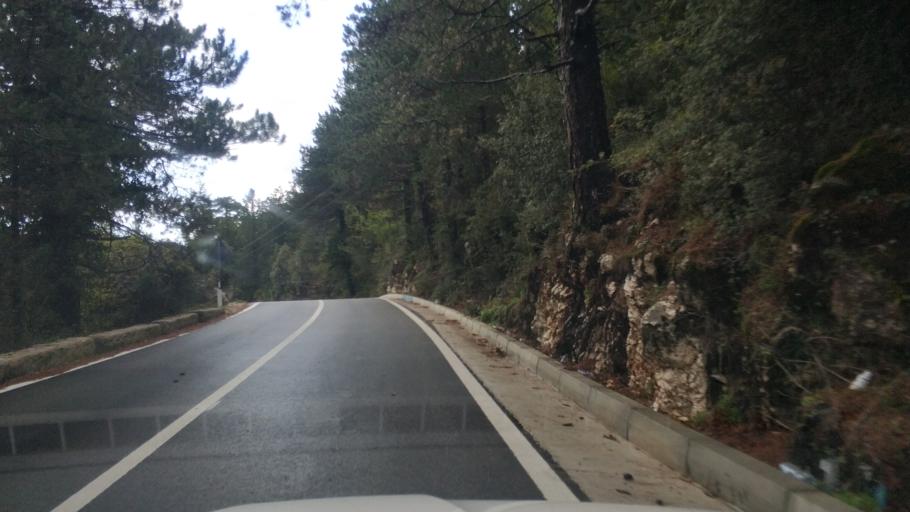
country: AL
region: Vlore
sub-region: Rrethi i Vlores
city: Brataj
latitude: 40.2168
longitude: 19.5791
